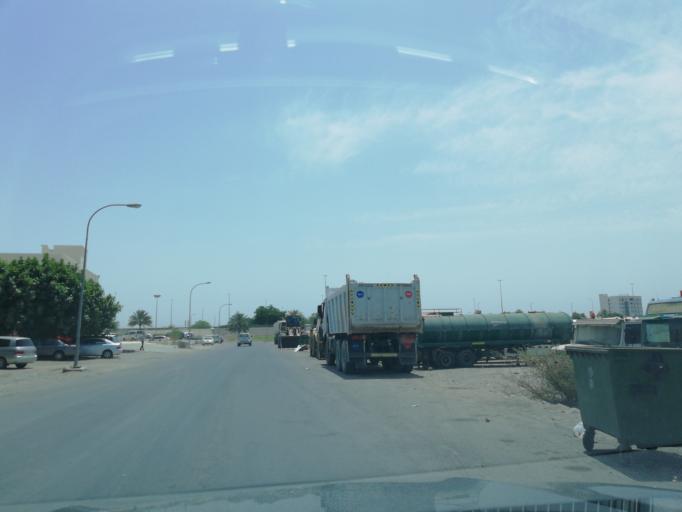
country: OM
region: Muhafazat Masqat
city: As Sib al Jadidah
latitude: 23.6577
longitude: 58.2027
